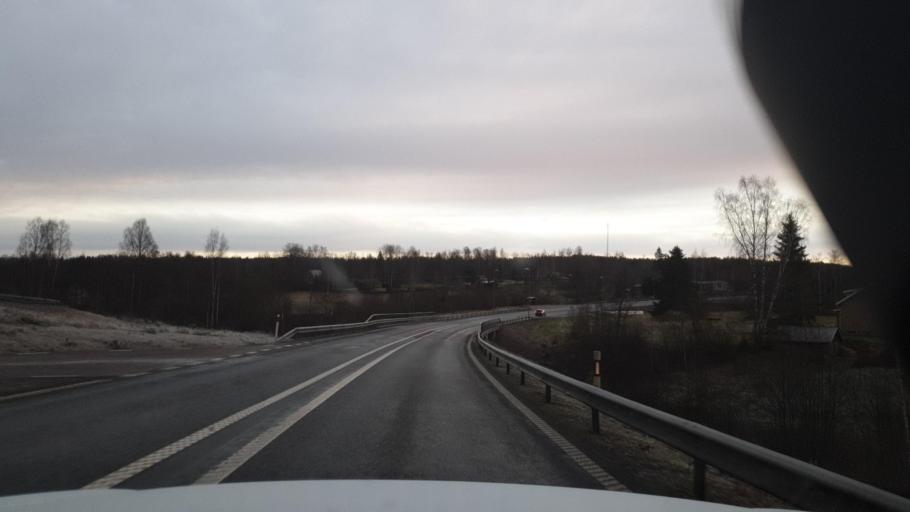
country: SE
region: Vaermland
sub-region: Eda Kommun
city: Amotfors
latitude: 59.7577
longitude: 12.4412
